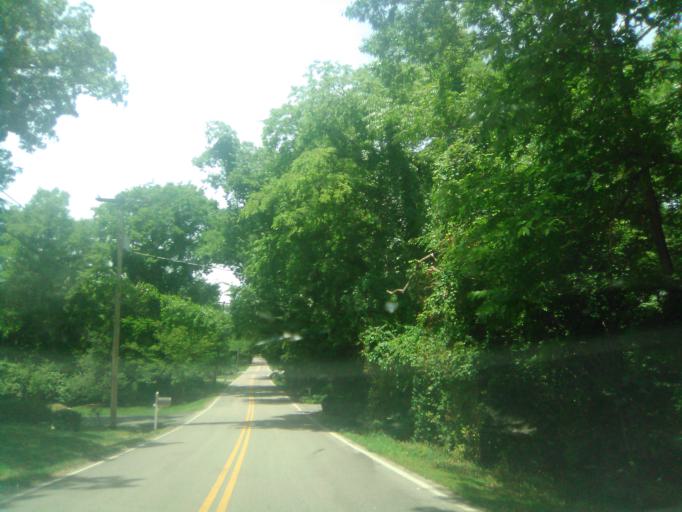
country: US
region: Tennessee
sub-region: Davidson County
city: Belle Meade
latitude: 36.0976
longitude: -86.8508
